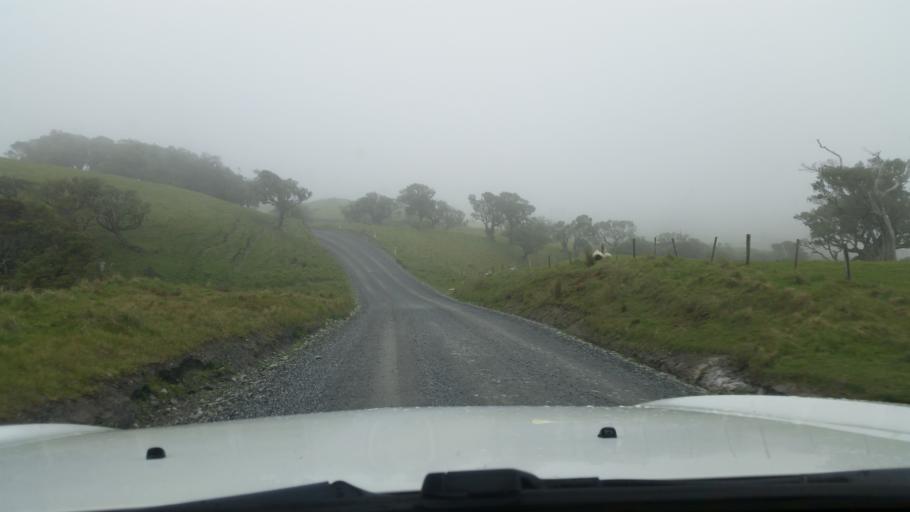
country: NZ
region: Chatham Islands
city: Waitangi
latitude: -43.8102
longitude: -176.5914
